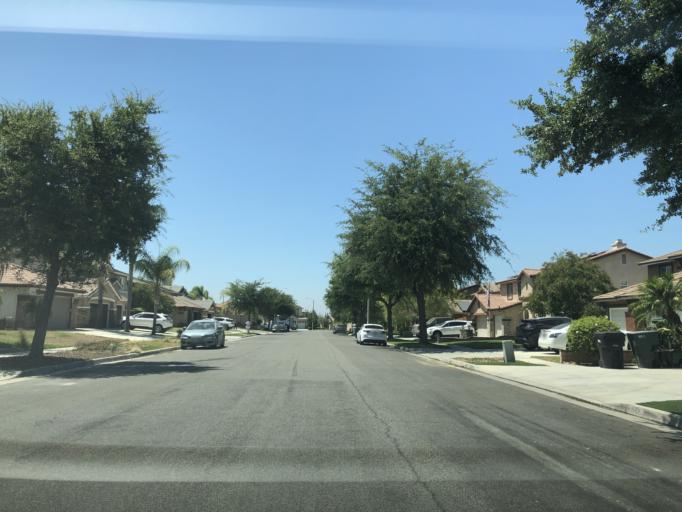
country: US
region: California
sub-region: Riverside County
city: Corona
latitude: 33.8499
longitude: -117.5799
